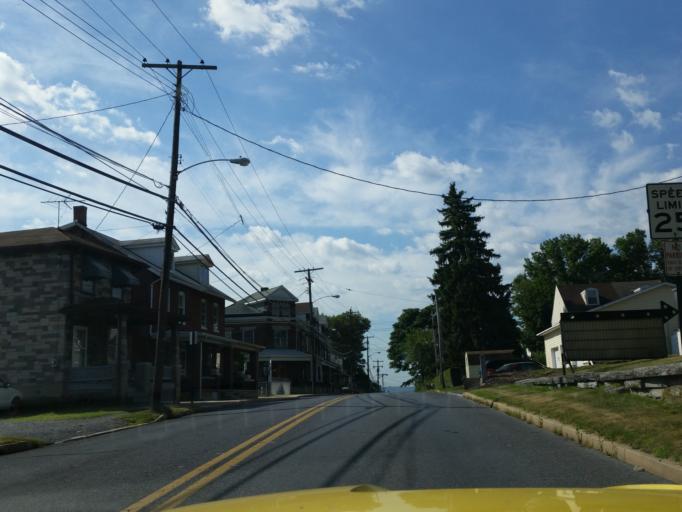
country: US
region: Pennsylvania
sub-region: Lebanon County
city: Sand Hill
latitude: 40.3522
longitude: -76.4235
